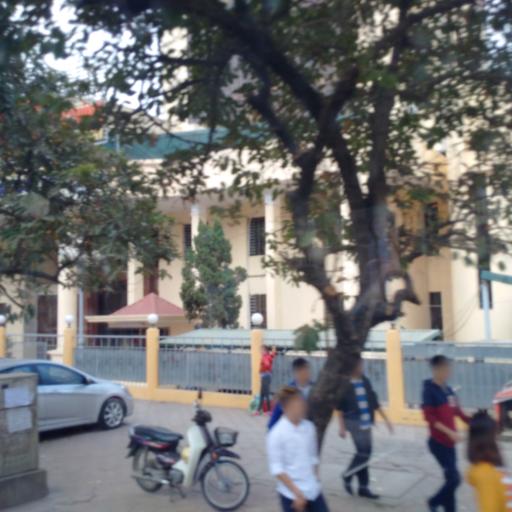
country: VN
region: Ha Noi
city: Cau Giay
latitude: 21.0461
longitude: 105.7939
